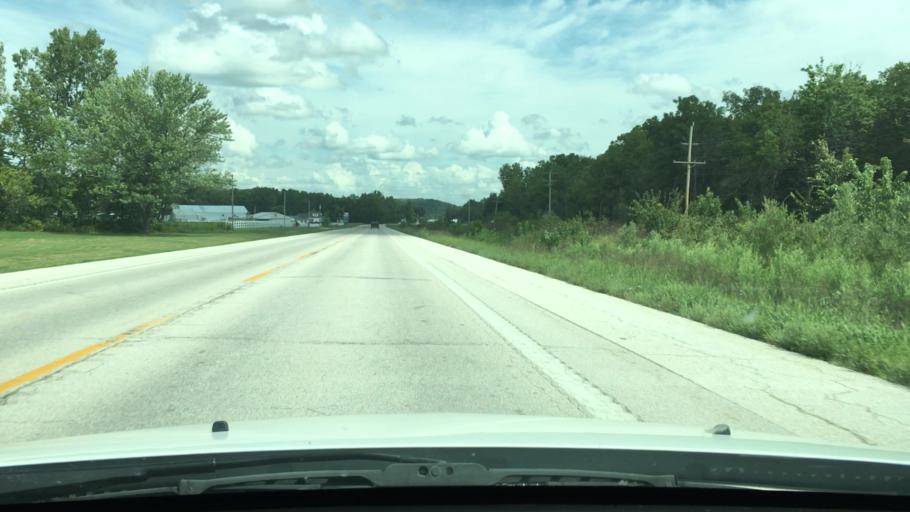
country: US
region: Missouri
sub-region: Pike County
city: Louisiana
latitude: 39.4055
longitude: -91.1061
